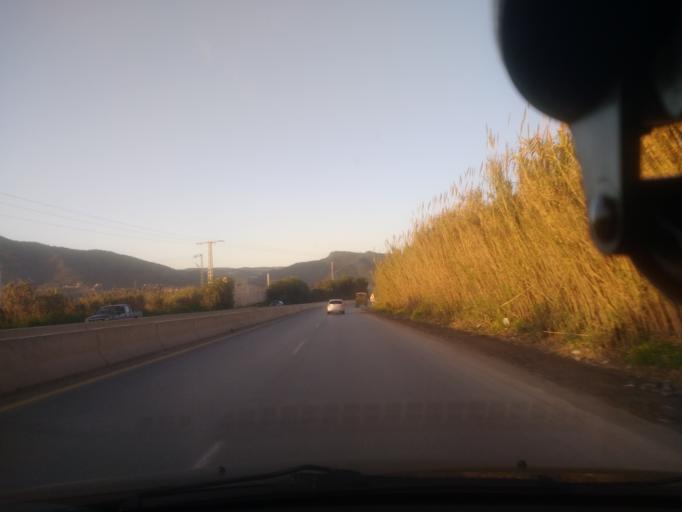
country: DZ
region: Tizi Ouzou
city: Tizi Ouzou
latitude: 36.7494
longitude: 4.0155
